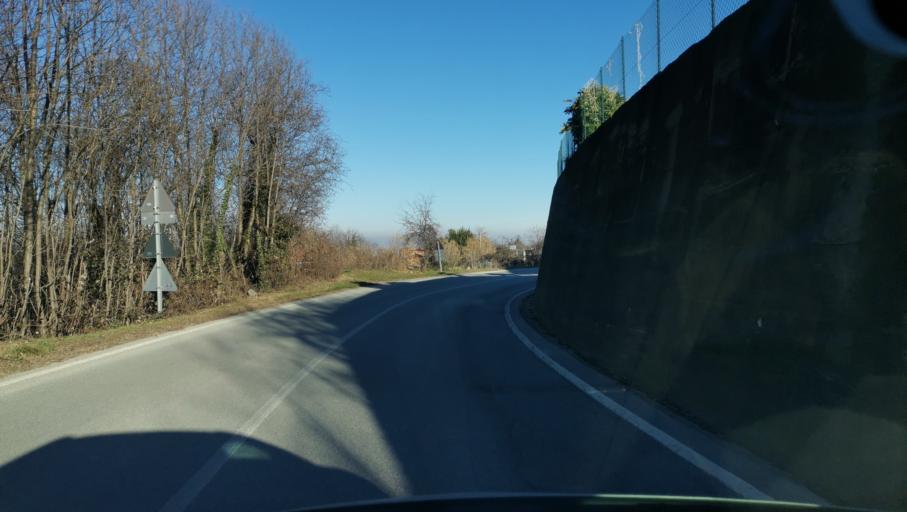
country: IT
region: Piedmont
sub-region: Provincia di Cuneo
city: Bagnolo Piemonte
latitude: 44.7538
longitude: 7.2877
